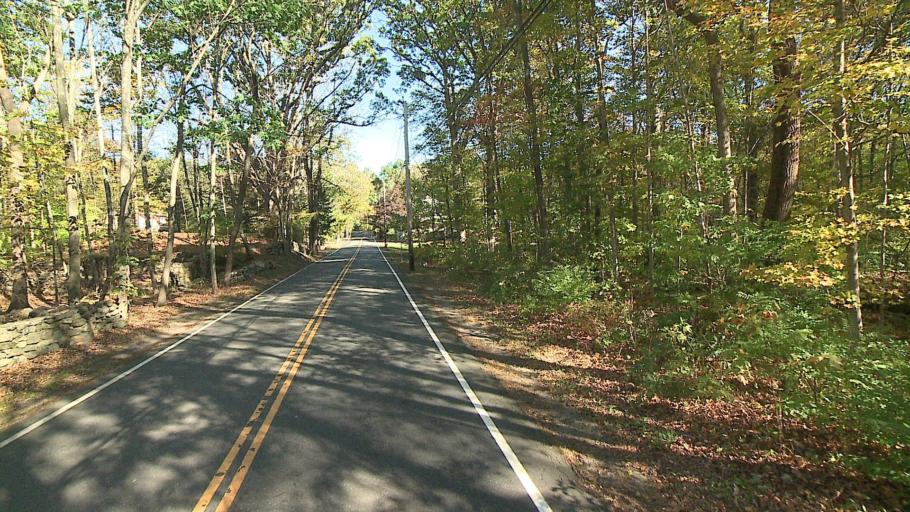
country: US
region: Connecticut
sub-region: Fairfield County
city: Trumbull
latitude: 41.2579
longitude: -73.3012
